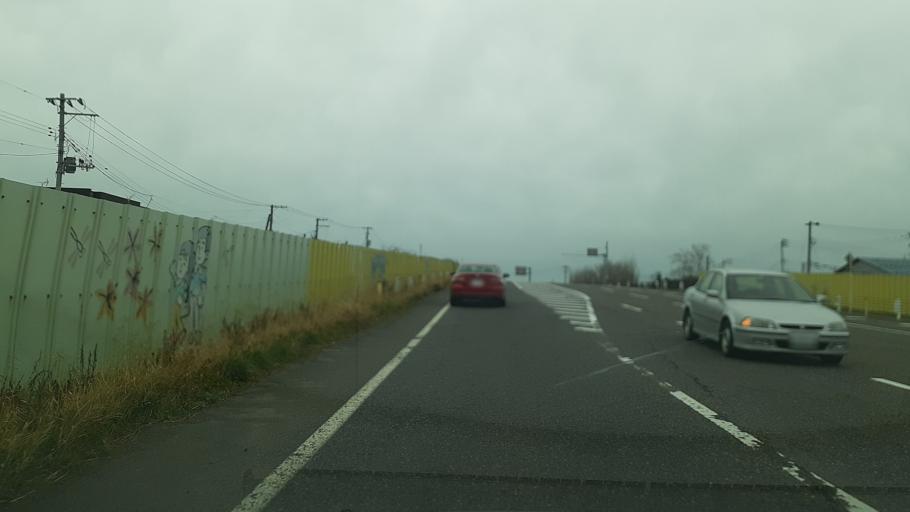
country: JP
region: Niigata
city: Niitsu-honcho
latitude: 37.7950
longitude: 139.1092
